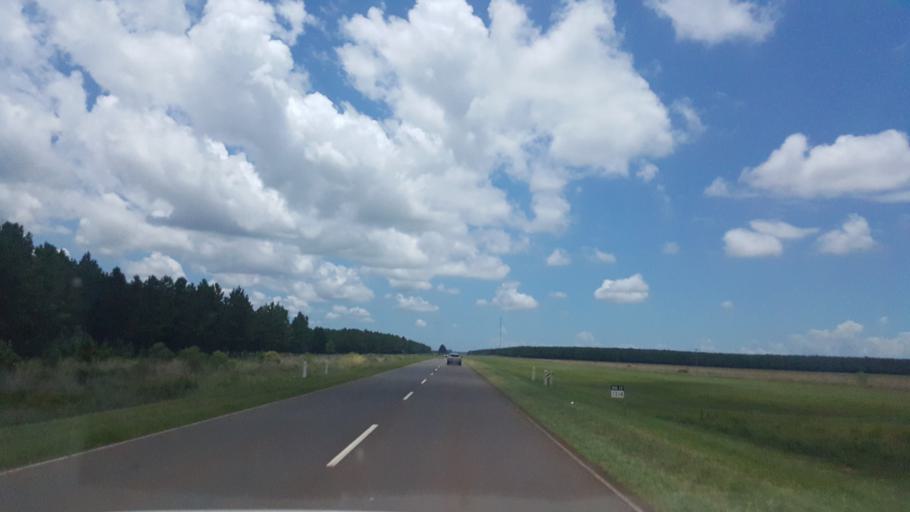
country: PY
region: Itapua
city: San Juan del Parana
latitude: -27.5141
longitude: -56.1436
